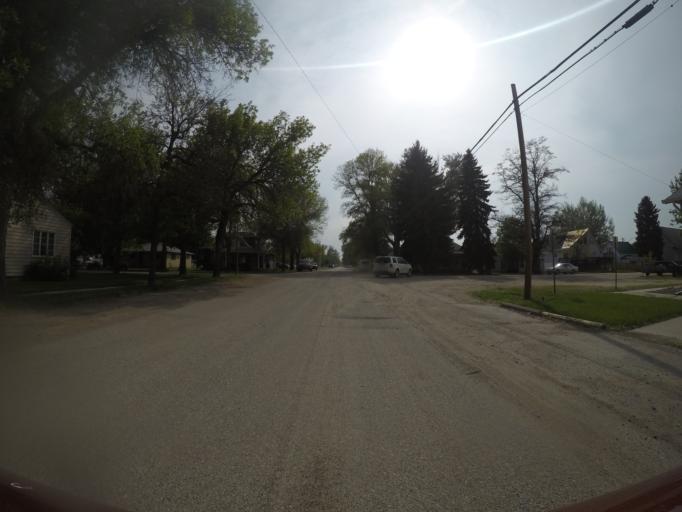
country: US
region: Montana
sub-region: Yellowstone County
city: Laurel
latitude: 45.4836
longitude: -108.9727
